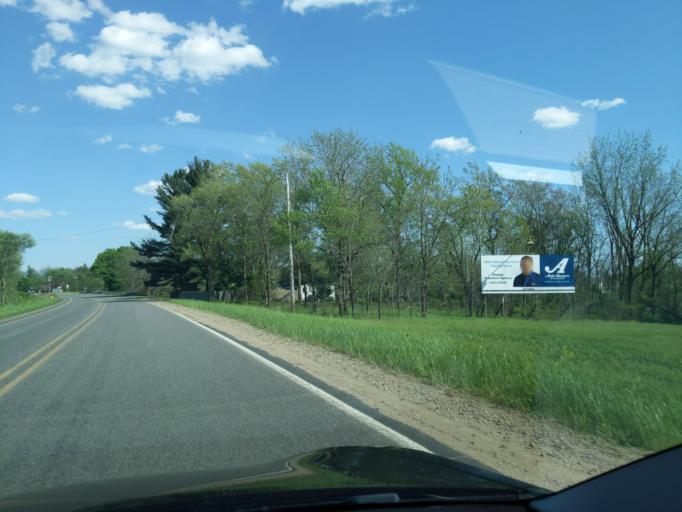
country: US
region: Michigan
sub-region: Ionia County
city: Lake Odessa
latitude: 42.7785
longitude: -85.1505
